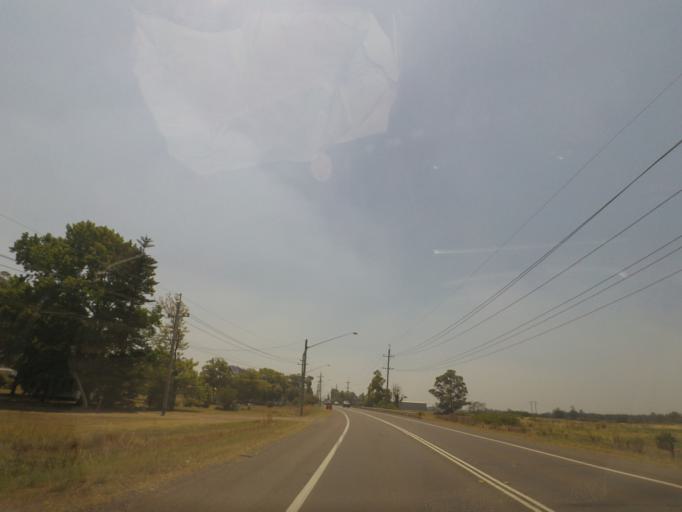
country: AU
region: New South Wales
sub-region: Newcastle
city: Mayfield West
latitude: -32.8268
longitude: 151.7374
